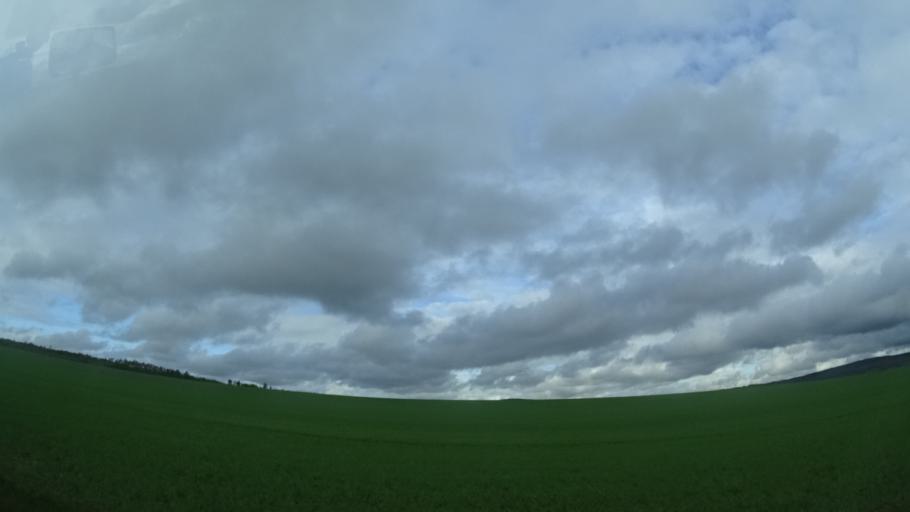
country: DE
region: Thuringia
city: Romhild
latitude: 50.3915
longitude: 10.5097
